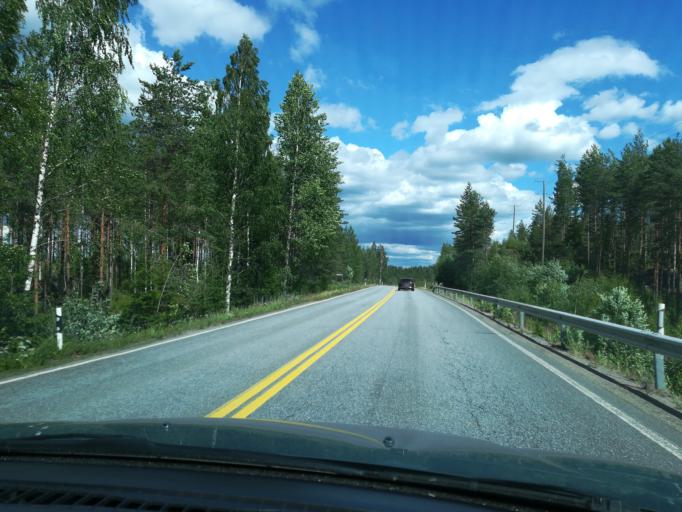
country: FI
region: Southern Savonia
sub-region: Mikkeli
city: Hirvensalmi
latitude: 61.6605
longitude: 26.9506
